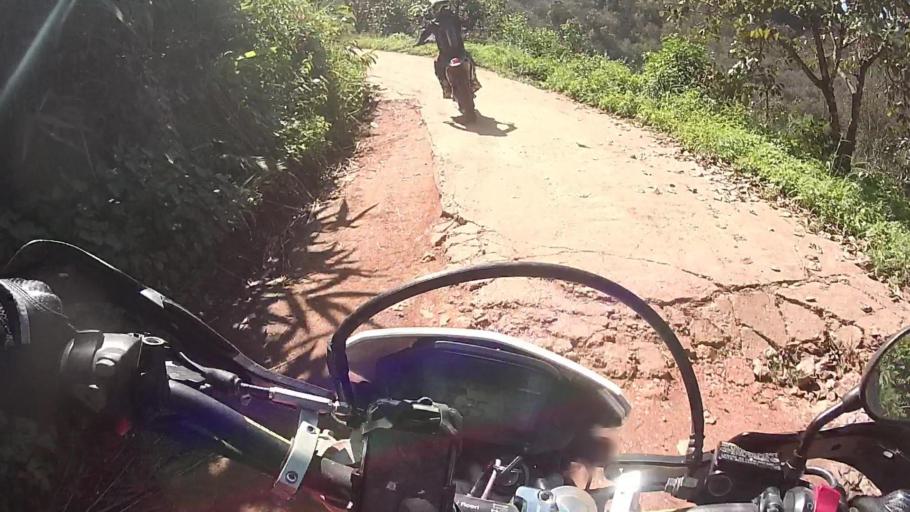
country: TH
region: Chiang Mai
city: Phrao
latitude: 19.4883
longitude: 99.3271
